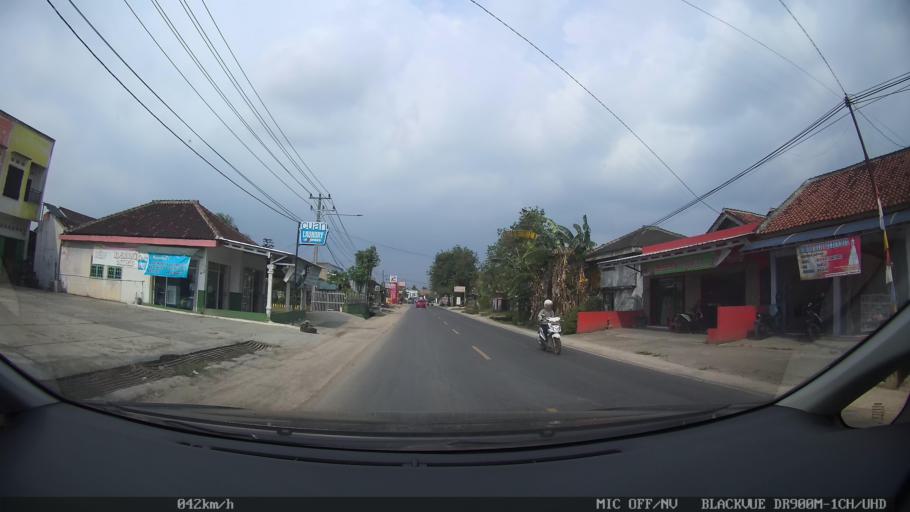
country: ID
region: Lampung
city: Gadingrejo
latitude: -5.3815
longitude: 105.0230
